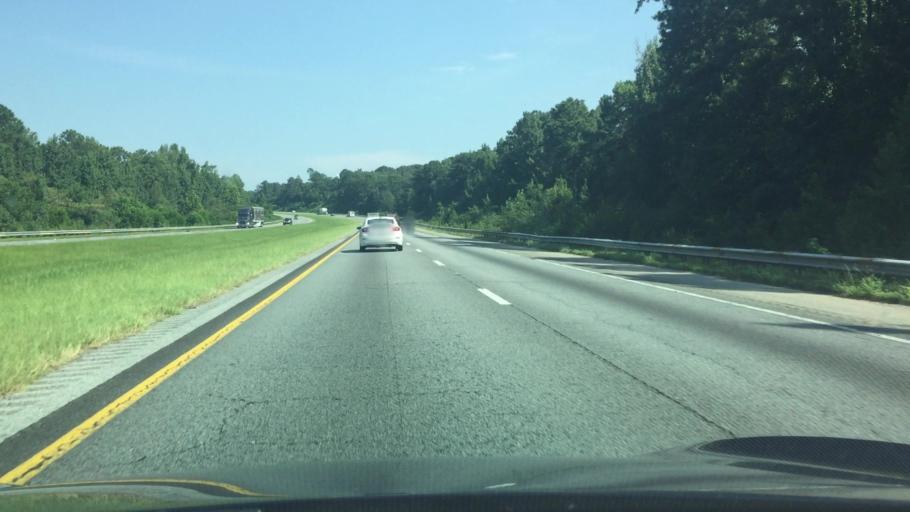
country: US
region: Alabama
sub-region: Autauga County
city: Pine Level
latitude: 32.6054
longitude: -86.4787
